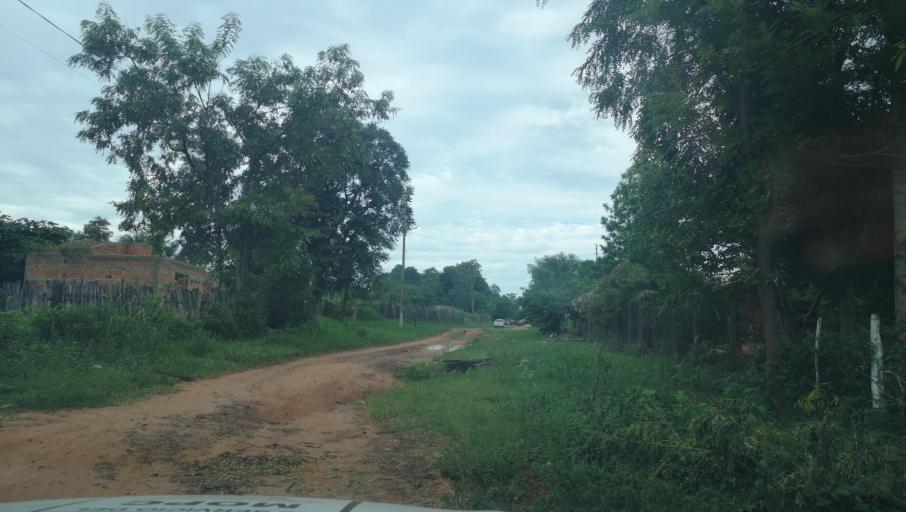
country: PY
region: San Pedro
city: Capiibary
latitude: -24.7426
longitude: -56.0269
